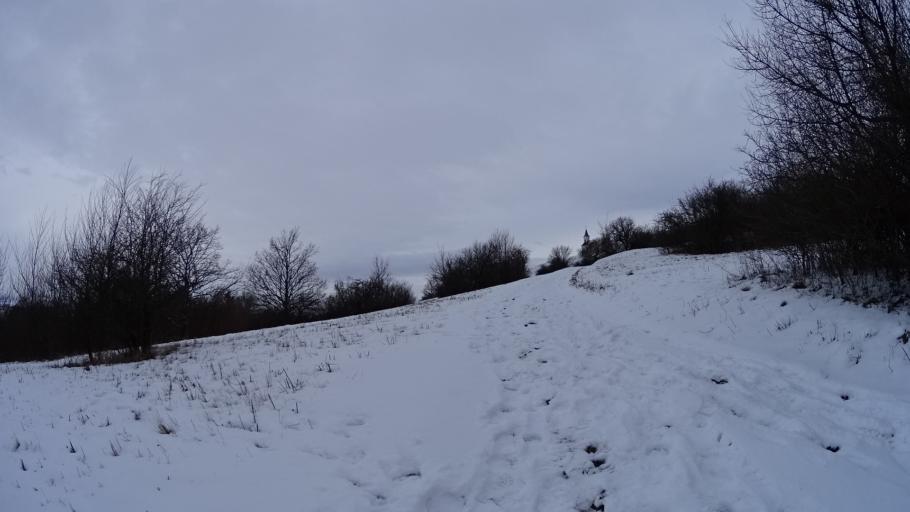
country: AT
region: Lower Austria
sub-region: Politischer Bezirk Korneuburg
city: Niederhollabrunn
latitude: 48.4276
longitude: 16.2896
